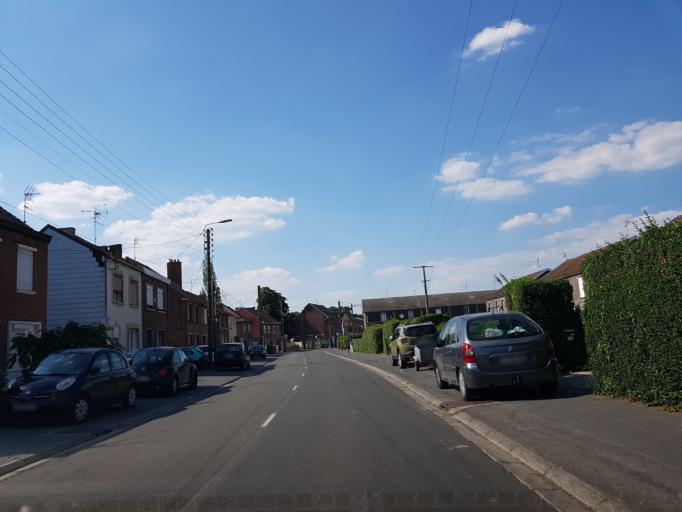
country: FR
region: Nord-Pas-de-Calais
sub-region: Departement du Nord
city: Lourches
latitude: 50.3158
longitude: 3.3432
